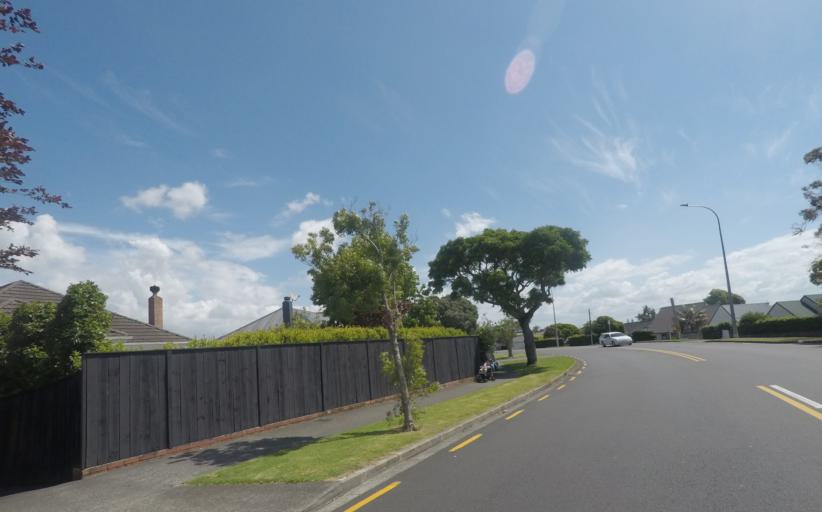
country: NZ
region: Auckland
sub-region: Auckland
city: Tamaki
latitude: -36.8735
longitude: 174.8294
